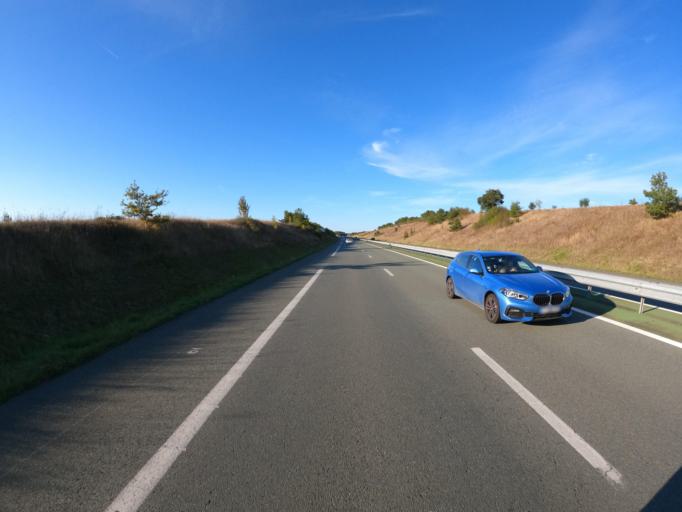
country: FR
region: Pays de la Loire
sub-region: Departement de Maine-et-Loire
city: Nuaille
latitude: 47.0969
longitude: -0.8248
